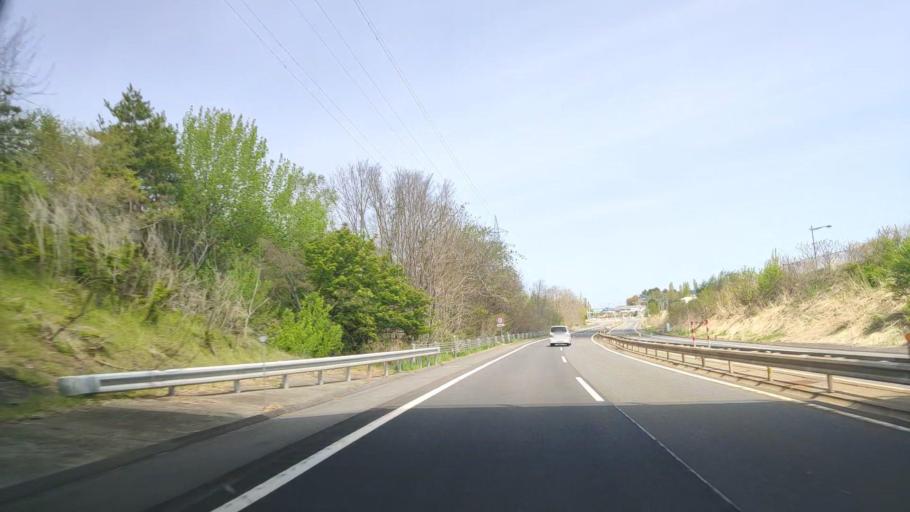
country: JP
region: Aomori
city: Hachinohe
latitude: 40.4821
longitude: 141.4600
